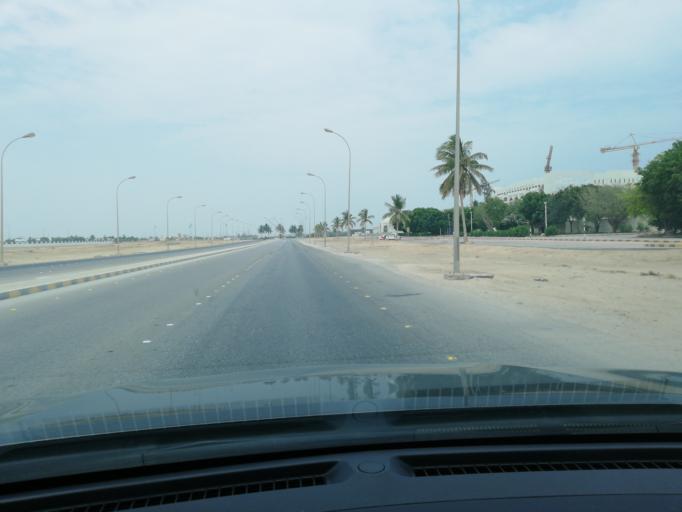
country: OM
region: Zufar
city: Salalah
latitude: 16.9818
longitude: 54.0133
